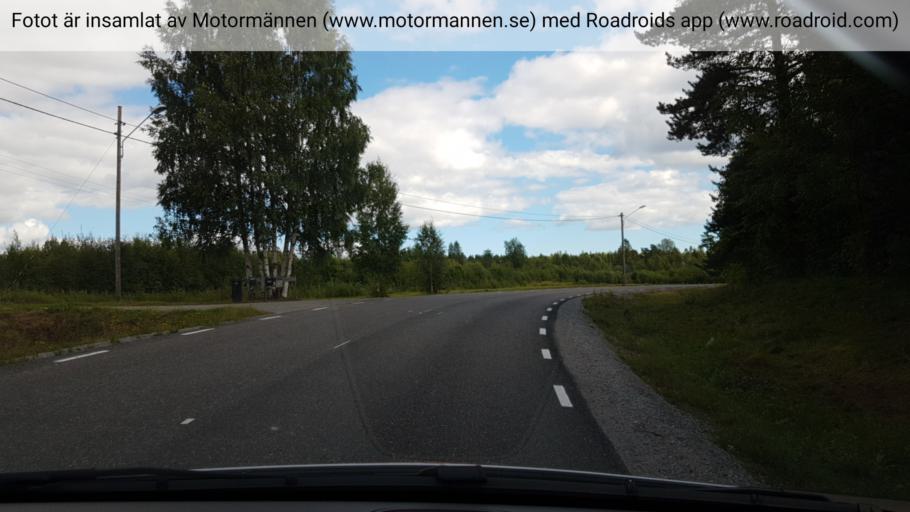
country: SE
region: Vaesterbotten
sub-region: Umea Kommun
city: Hoernefors
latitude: 63.6862
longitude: 19.8965
